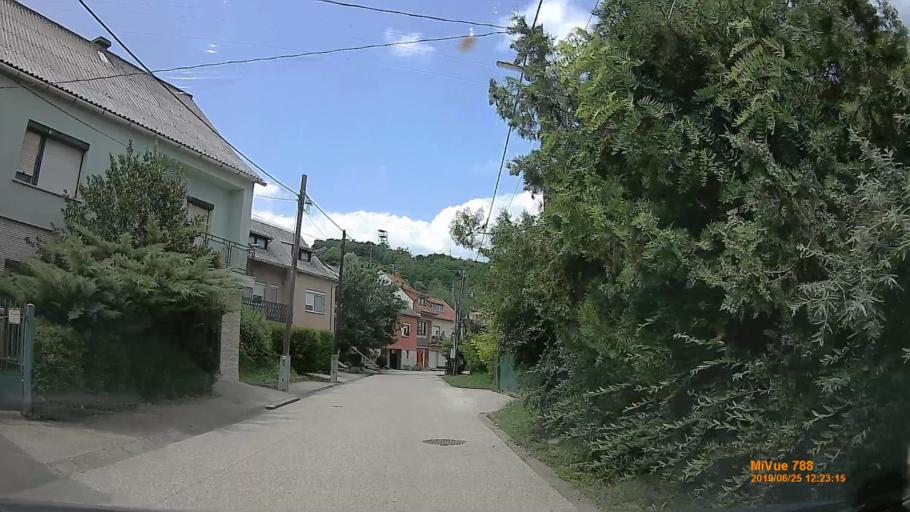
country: HU
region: Komarom-Esztergom
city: Dorog
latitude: 47.7169
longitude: 18.7290
